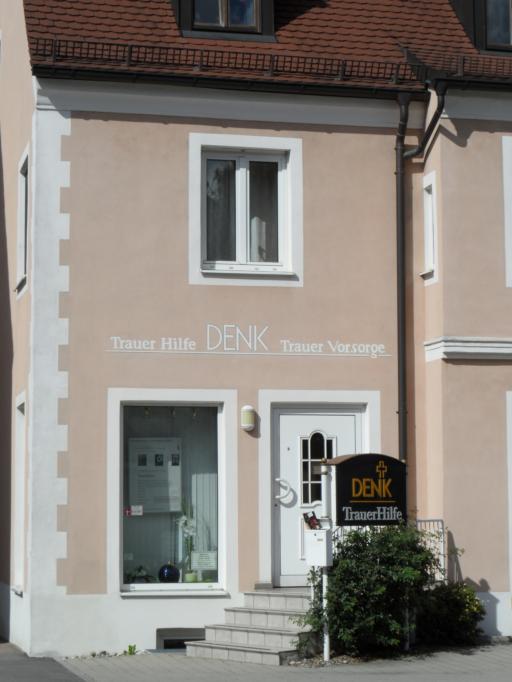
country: DE
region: Bavaria
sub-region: Upper Bavaria
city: Pfaffenhofen an der Ilm
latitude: 48.5276
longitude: 11.5119
